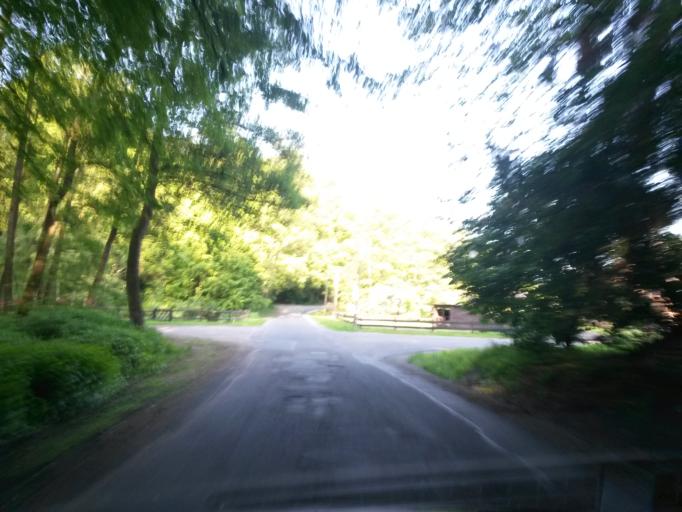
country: DE
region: North Rhine-Westphalia
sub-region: Regierungsbezirk Koln
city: Much
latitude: 50.8959
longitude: 7.3539
